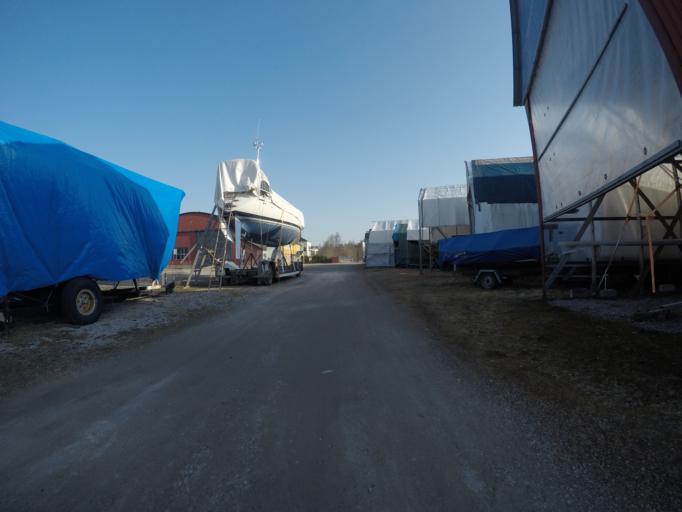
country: SE
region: Vaestmanland
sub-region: Kungsors Kommun
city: Kungsoer
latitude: 59.4298
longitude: 16.1055
